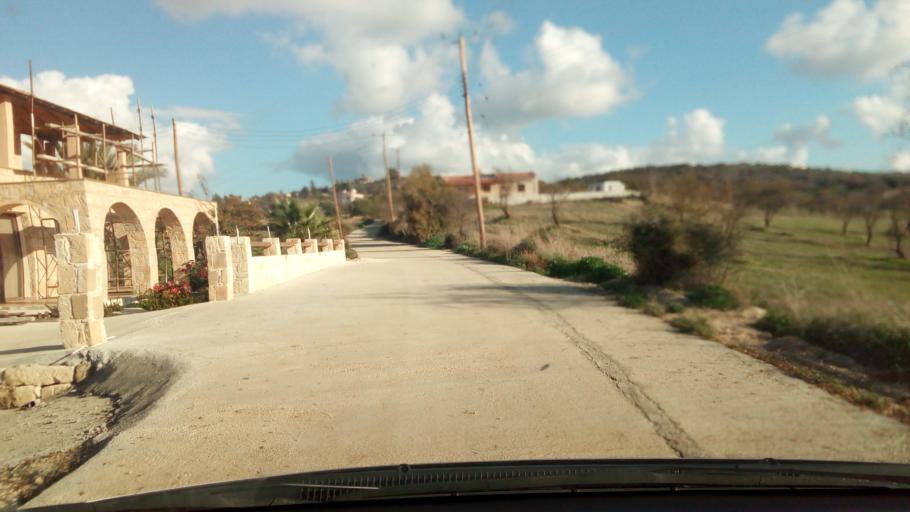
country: CY
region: Pafos
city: Polis
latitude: 34.9407
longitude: 32.4963
